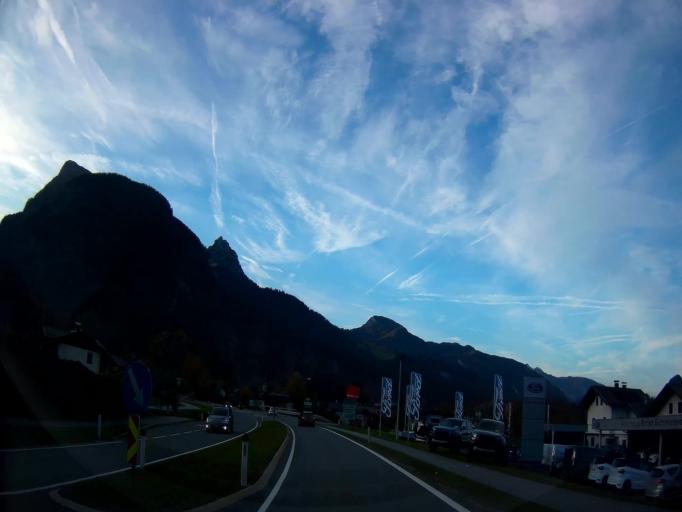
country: AT
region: Salzburg
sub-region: Politischer Bezirk Zell am See
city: Lofer
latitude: 47.5821
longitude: 12.6985
